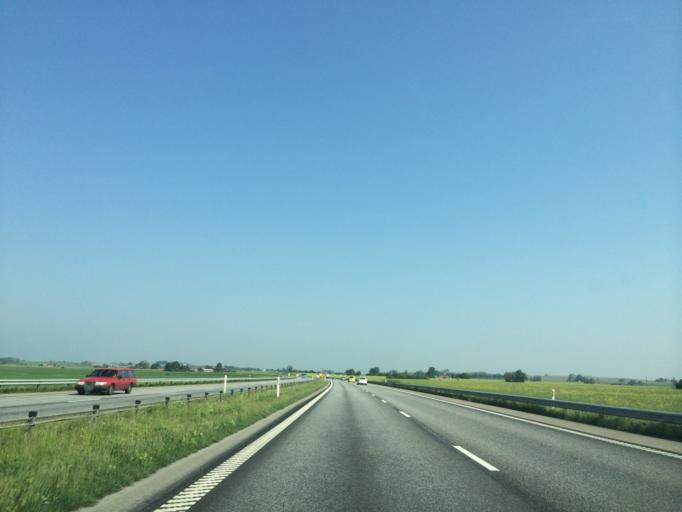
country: SE
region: Skane
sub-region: Landskrona
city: Landskrona
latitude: 55.9004
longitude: 12.8659
